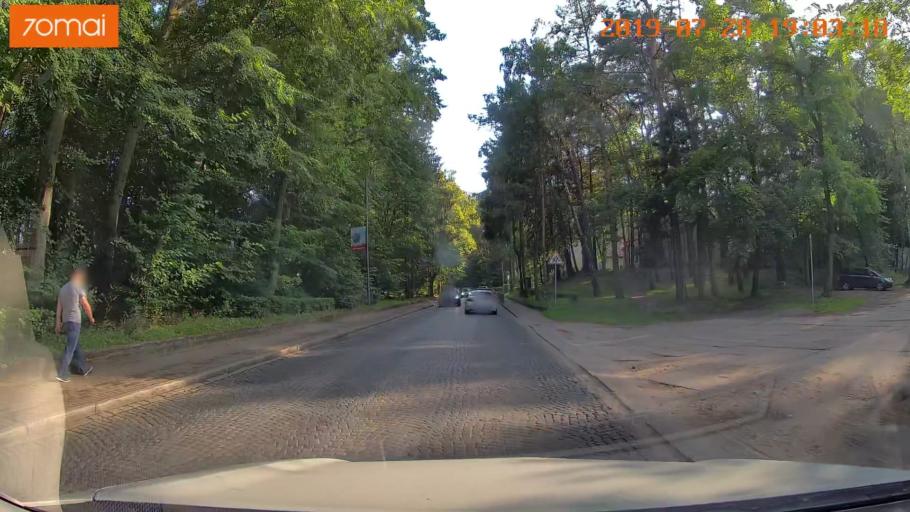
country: RU
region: Kaliningrad
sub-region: Gorod Svetlogorsk
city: Svetlogorsk
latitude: 54.9362
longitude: 20.1625
